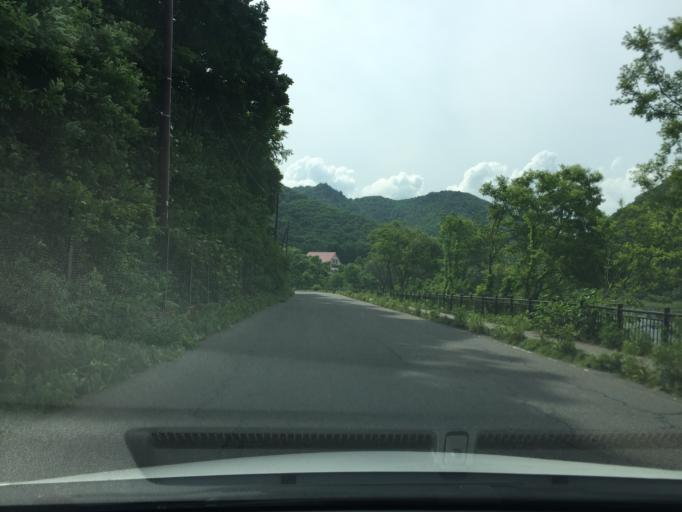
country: JP
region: Fukushima
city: Inawashiro
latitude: 37.7183
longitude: 140.0369
